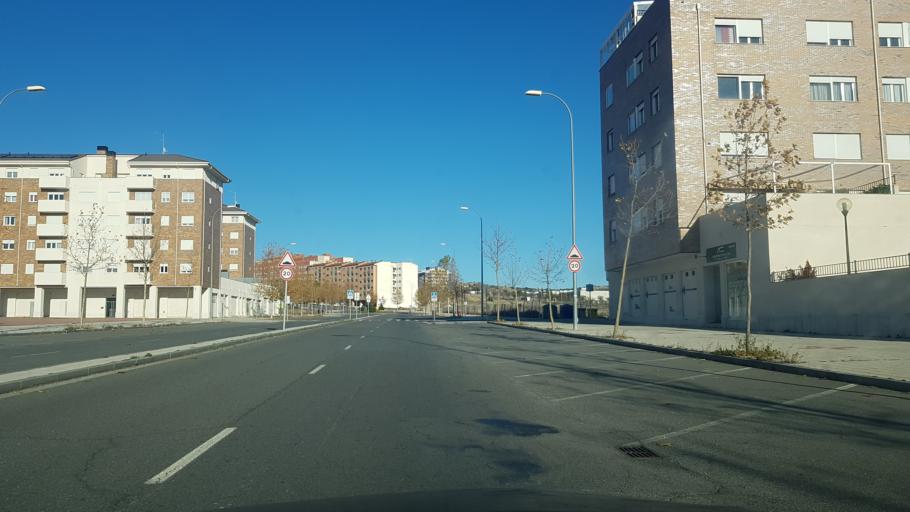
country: ES
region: Castille and Leon
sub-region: Provincia de Avila
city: Avila
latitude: 40.6455
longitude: -4.6805
